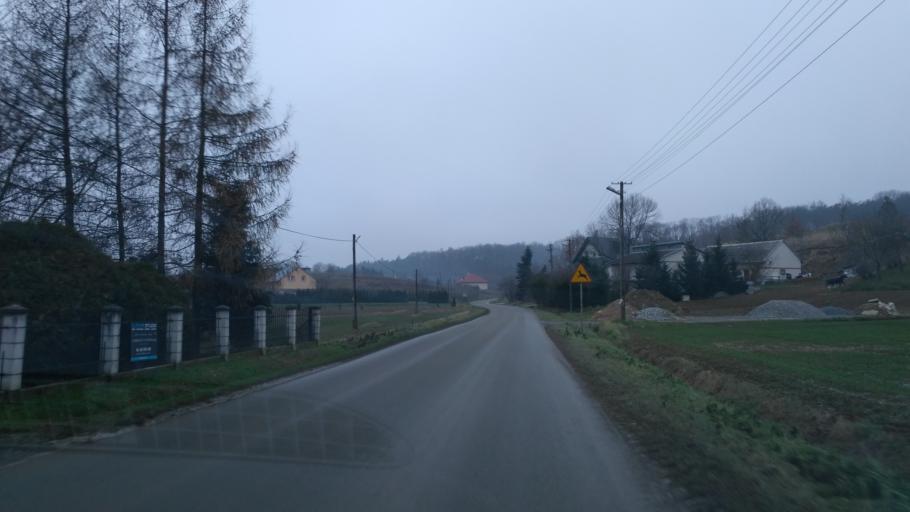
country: PL
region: Subcarpathian Voivodeship
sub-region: Powiat przeworski
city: Zarzecze
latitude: 49.9924
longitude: 22.5221
